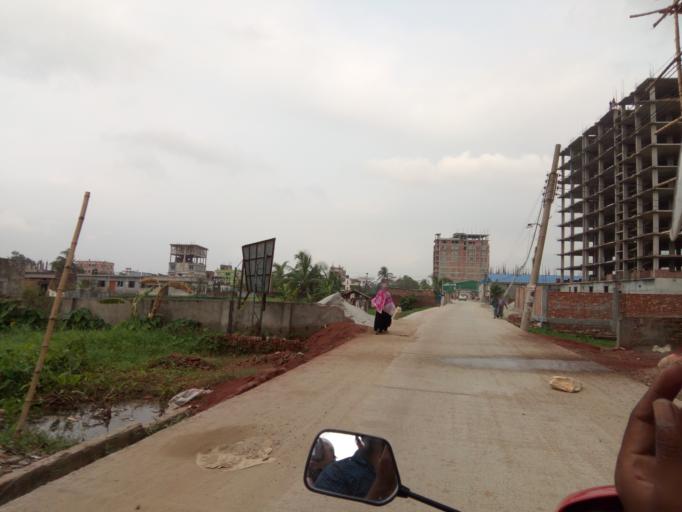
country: BD
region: Dhaka
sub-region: Dhaka
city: Dhaka
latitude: 23.7020
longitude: 90.4735
